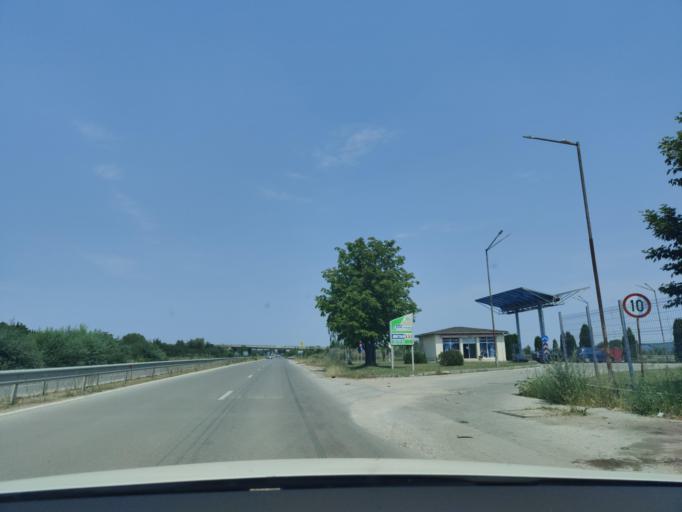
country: BG
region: Montana
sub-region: Obshtina Montana
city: Montana
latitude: 43.4327
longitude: 23.2323
